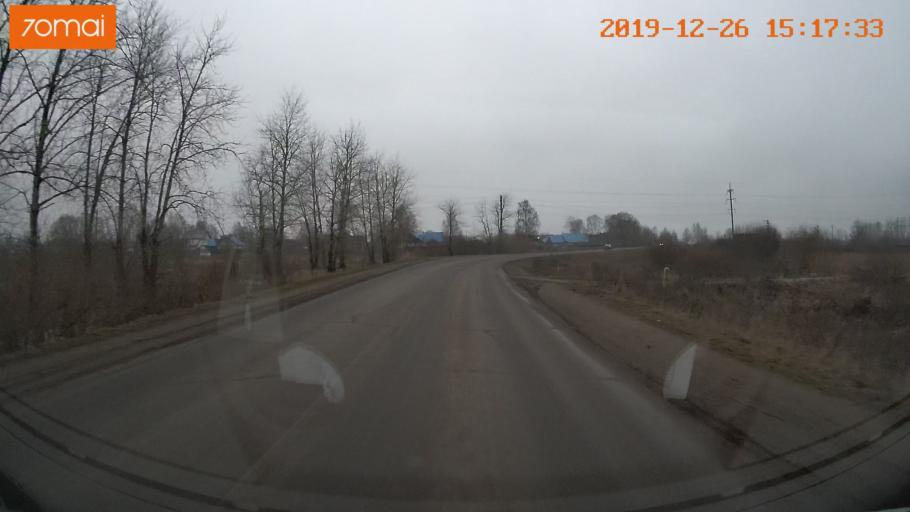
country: RU
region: Jaroslavl
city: Rybinsk
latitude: 58.0759
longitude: 38.8506
